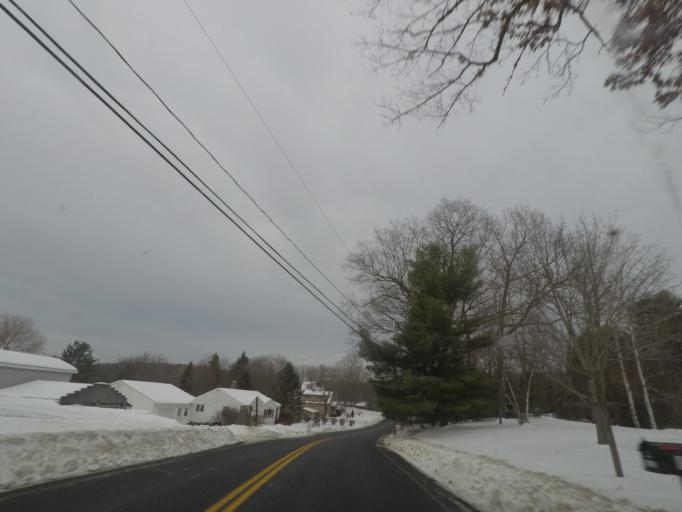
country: US
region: New York
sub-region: Rensselaer County
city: Castleton-on-Hudson
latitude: 42.5208
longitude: -73.6851
